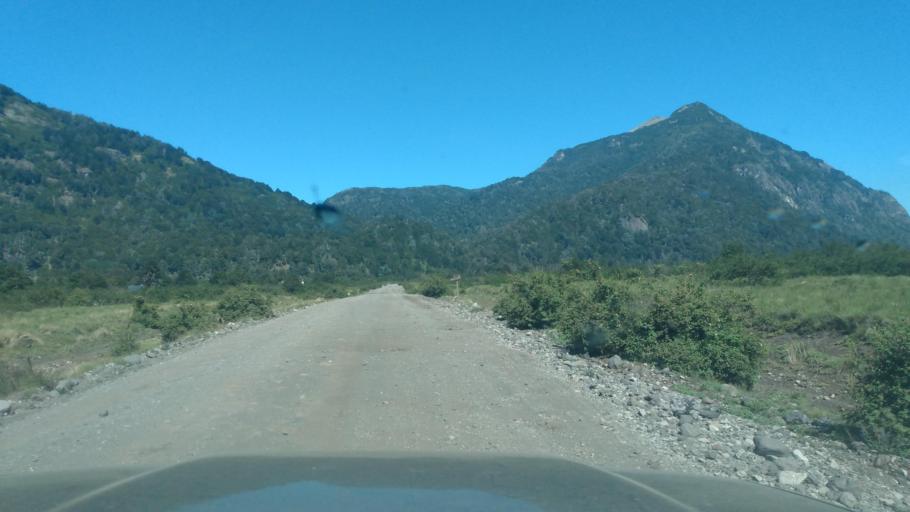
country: AR
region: Neuquen
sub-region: Departamento de Lacar
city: San Martin de los Andes
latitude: -39.7459
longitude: -71.5145
